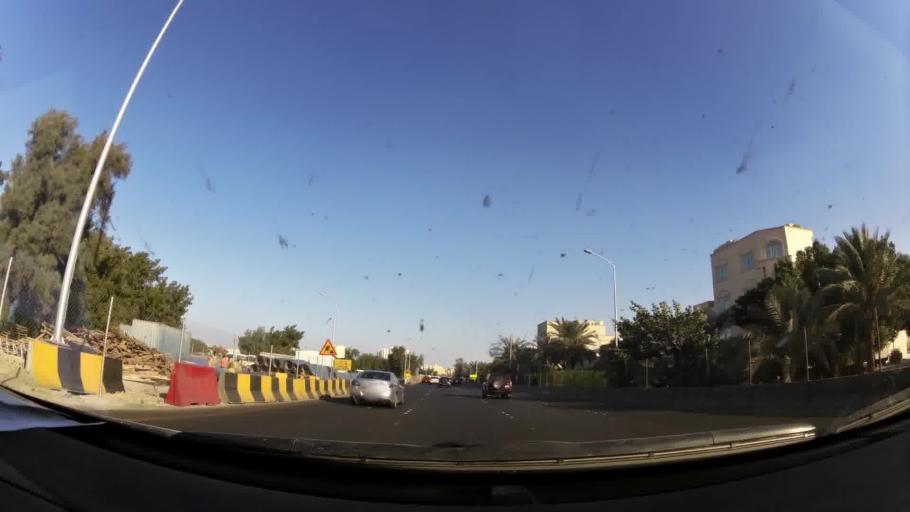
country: KW
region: Mubarak al Kabir
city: Sabah as Salim
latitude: 29.2641
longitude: 48.0619
